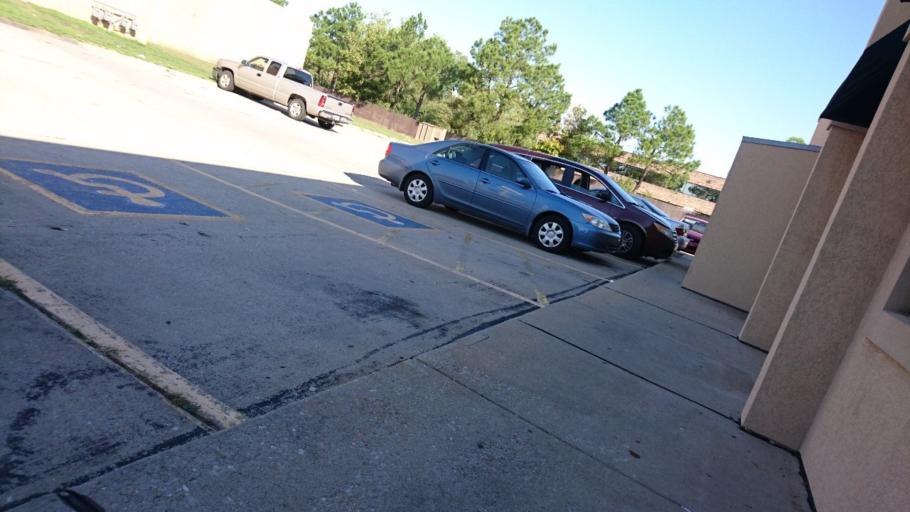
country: US
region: Oklahoma
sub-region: Oklahoma County
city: Warr Acres
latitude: 35.5120
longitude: -97.5916
